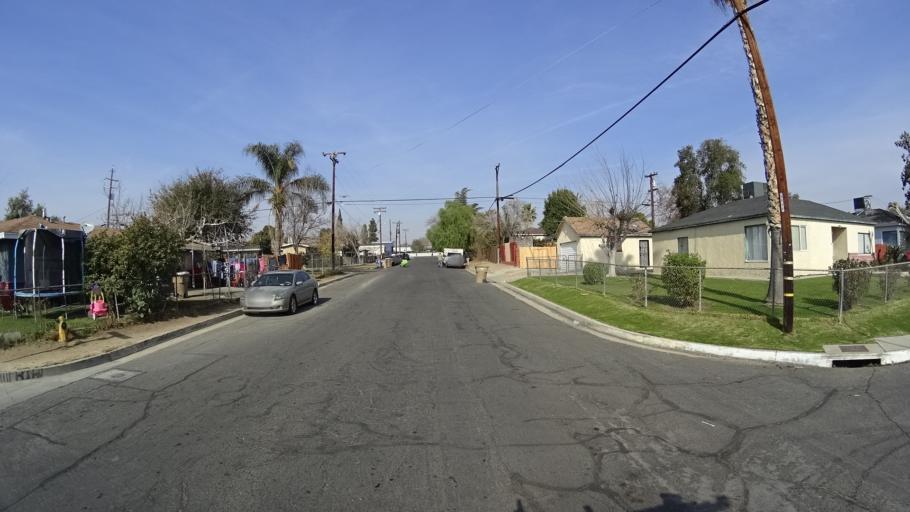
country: US
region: California
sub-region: Kern County
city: Bakersfield
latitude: 35.3957
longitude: -118.9807
